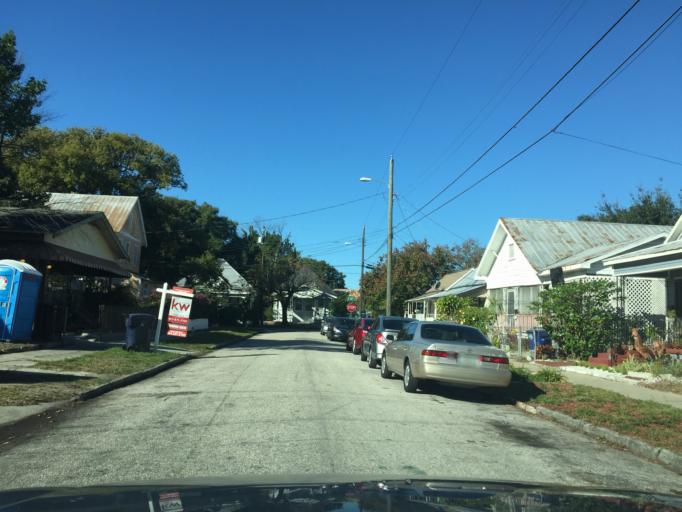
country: US
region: Florida
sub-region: Hillsborough County
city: Tampa
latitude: 27.9662
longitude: -82.4484
